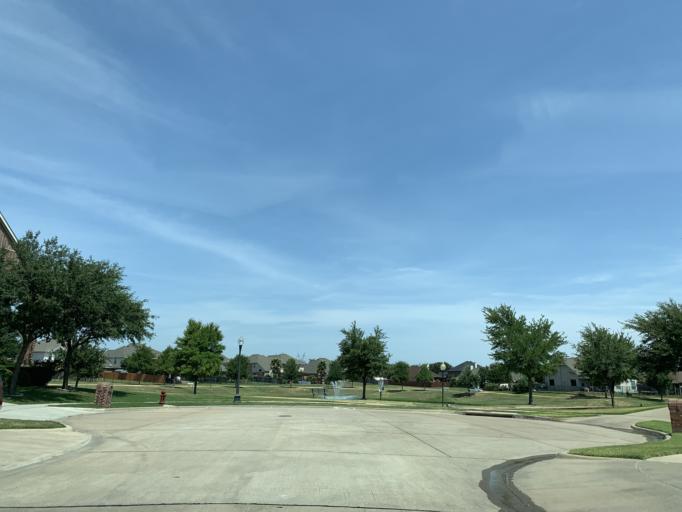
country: US
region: Texas
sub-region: Dallas County
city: Cedar Hill
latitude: 32.6405
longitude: -97.0450
